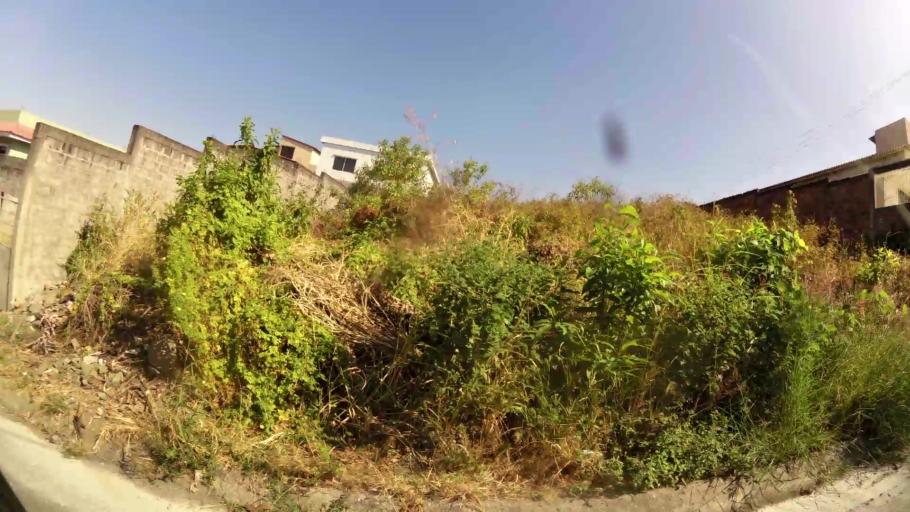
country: EC
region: Guayas
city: Guayaquil
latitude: -2.1832
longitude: -79.9160
